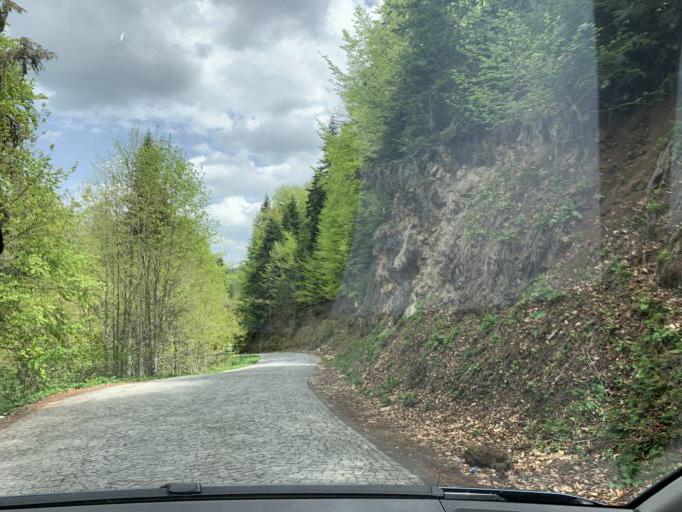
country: TR
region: Zonguldak
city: Egerci
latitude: 40.9294
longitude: 31.7442
